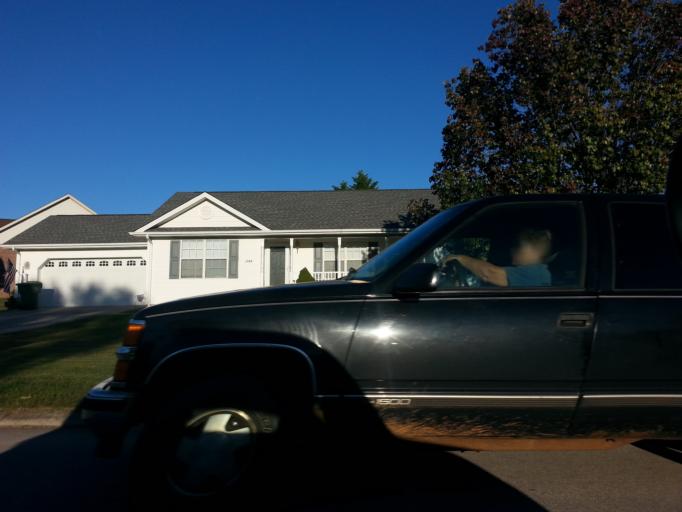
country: US
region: Tennessee
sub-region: Blount County
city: Eagleton Village
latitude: 35.7713
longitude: -83.9190
